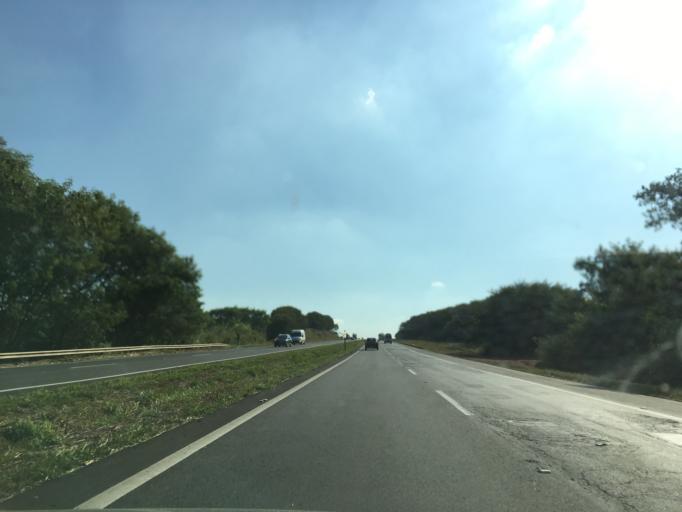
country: BR
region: Sao Paulo
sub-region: Piracicaba
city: Piracicaba
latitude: -22.7261
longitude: -47.5625
